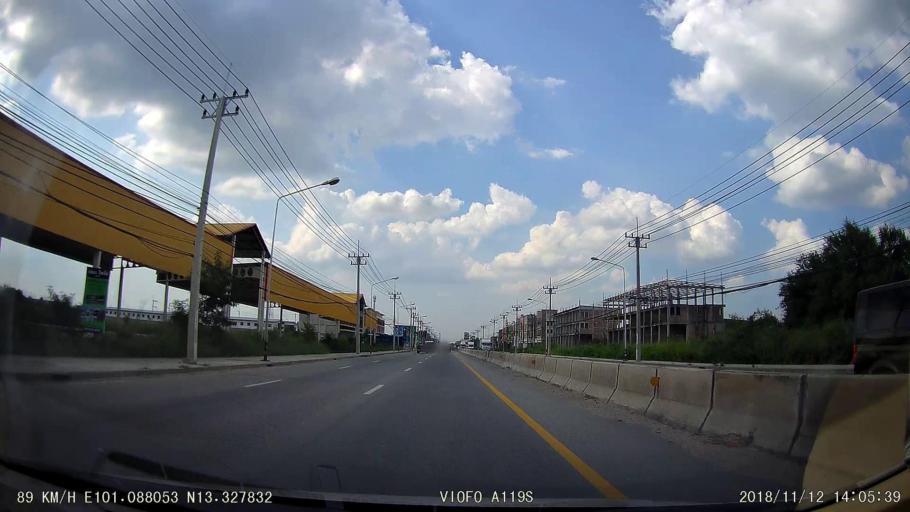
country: TH
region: Chon Buri
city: Ban Bueng
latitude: 13.3281
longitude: 101.0877
